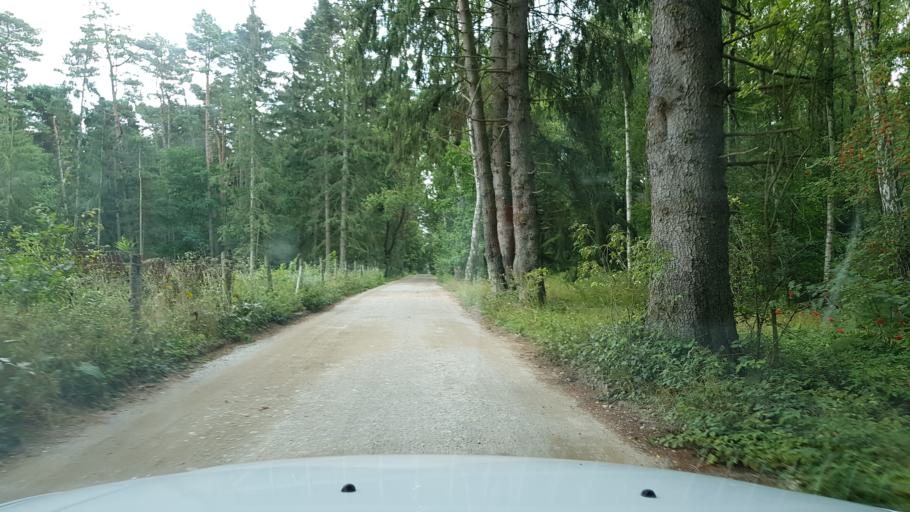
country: PL
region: West Pomeranian Voivodeship
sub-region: Powiat gryficki
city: Pobierowo
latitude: 54.0494
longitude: 14.9056
